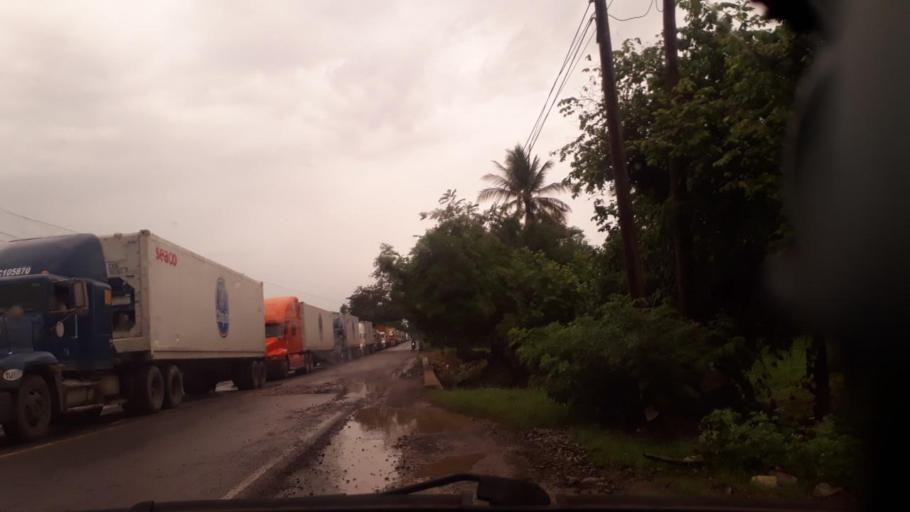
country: SV
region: Ahuachapan
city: San Francisco Menendez
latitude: 13.8798
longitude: -90.1107
